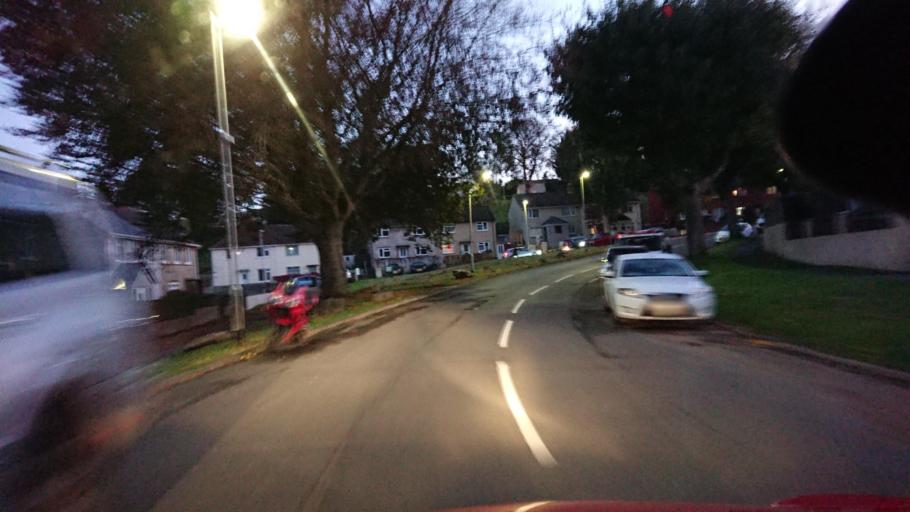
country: GB
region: England
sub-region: Plymouth
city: Plymstock
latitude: 50.3887
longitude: -4.0953
